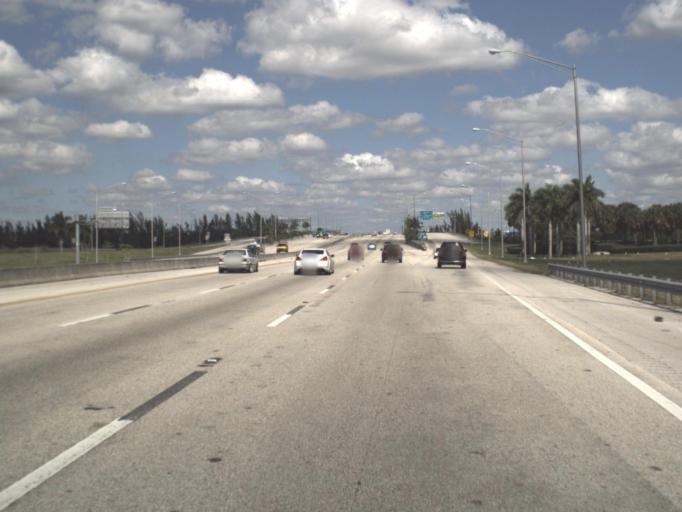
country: US
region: Florida
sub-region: Miami-Dade County
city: Sweetwater
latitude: 25.7769
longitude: -80.3858
